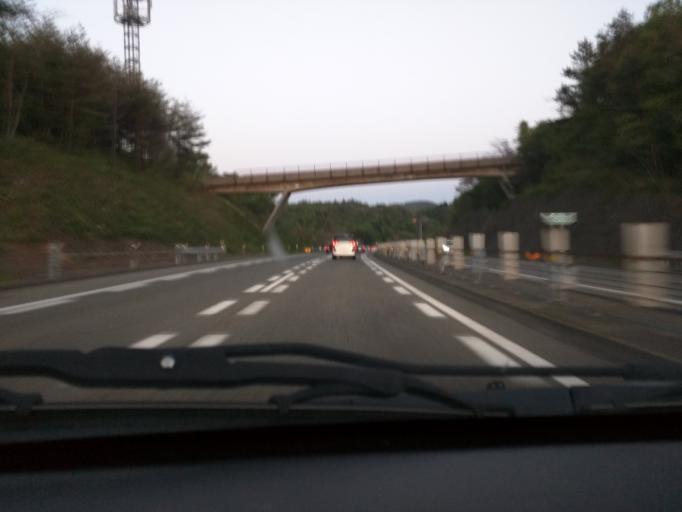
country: JP
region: Niigata
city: Kashiwazaki
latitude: 37.3473
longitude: 138.5098
